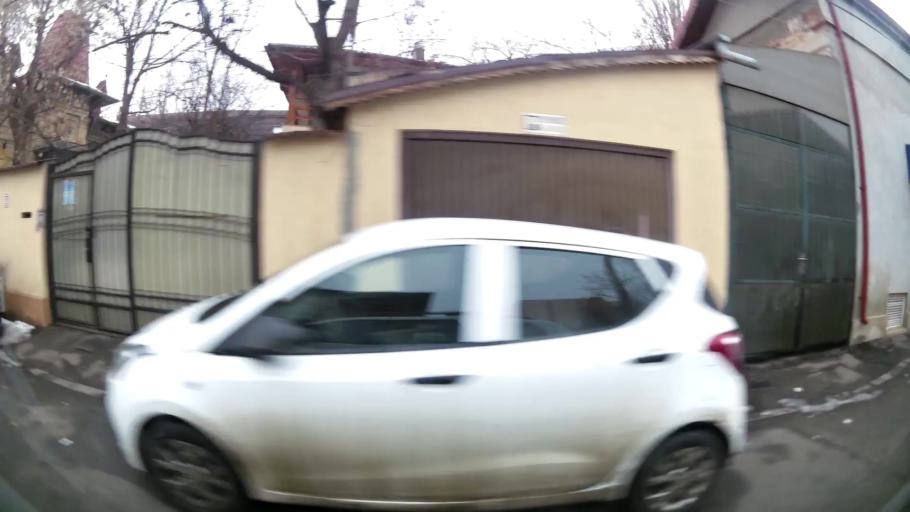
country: RO
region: Bucuresti
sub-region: Municipiul Bucuresti
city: Bucharest
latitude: 44.4378
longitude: 26.1270
